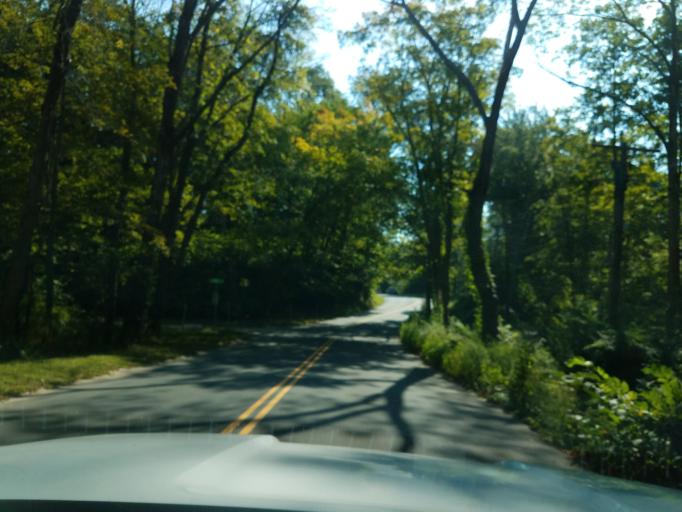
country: US
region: Connecticut
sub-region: Fairfield County
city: Newtown
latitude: 41.3703
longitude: -73.3366
